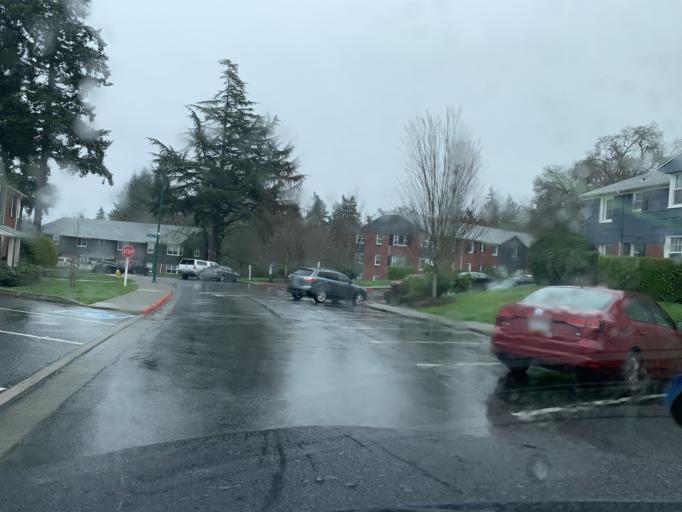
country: US
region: Washington
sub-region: King County
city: Mercer Island
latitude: 47.5787
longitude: -122.2195
